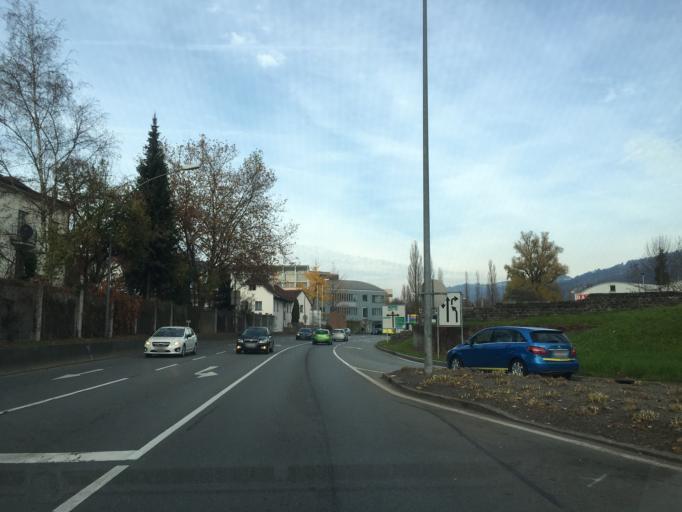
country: AT
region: Vorarlberg
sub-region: Politischer Bezirk Bregenz
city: Bregenz
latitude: 47.5002
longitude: 9.7353
